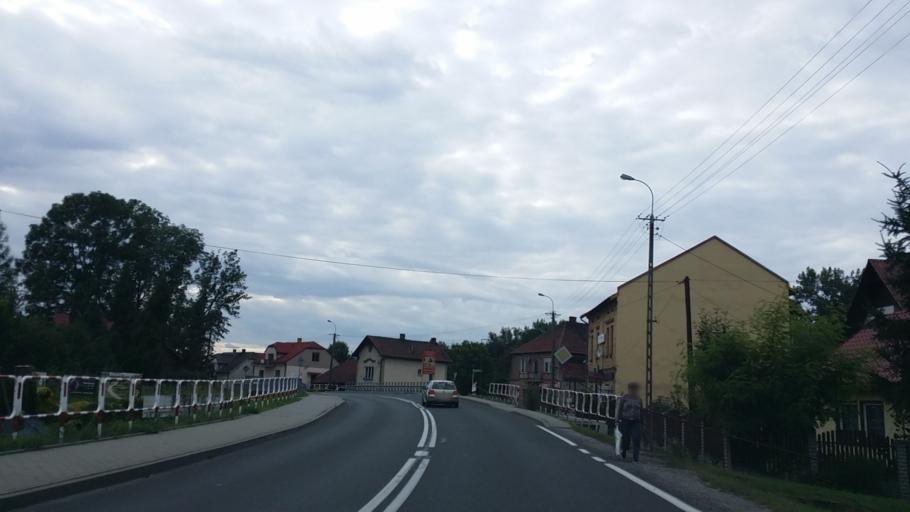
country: PL
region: Lesser Poland Voivodeship
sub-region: Powiat wadowicki
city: Brzeznica
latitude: 49.9659
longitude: 19.6337
